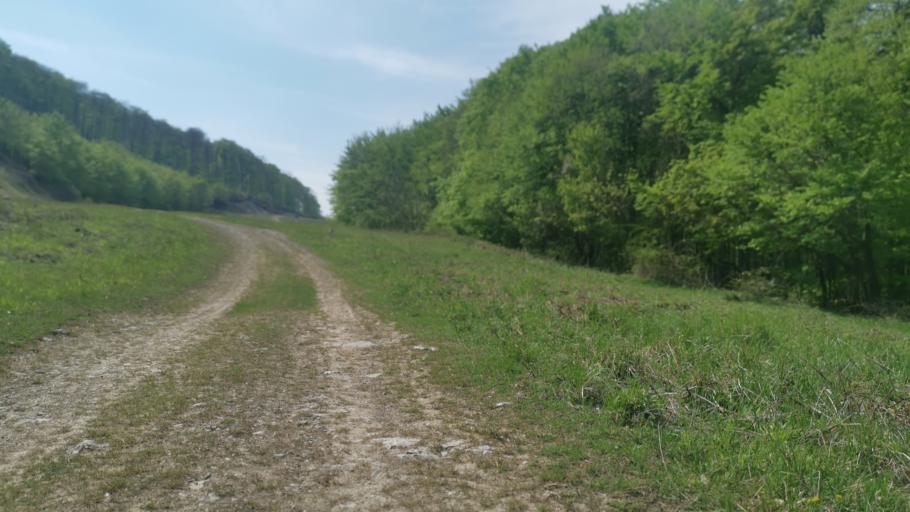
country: SK
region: Trnavsky
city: Smolenice
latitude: 48.5318
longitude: 17.4170
